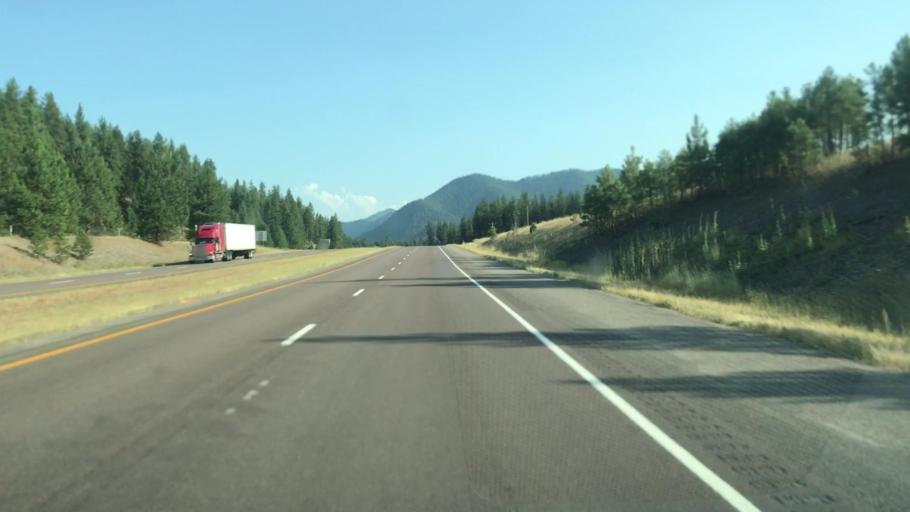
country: US
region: Montana
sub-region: Mineral County
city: Superior
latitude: 47.0651
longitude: -114.7642
